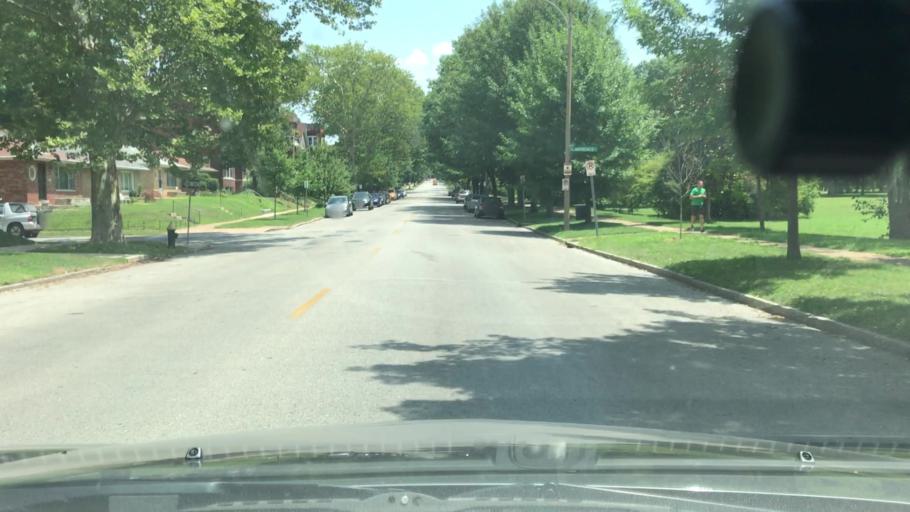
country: US
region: Missouri
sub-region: City of Saint Louis
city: St. Louis
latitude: 38.6080
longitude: -90.2496
